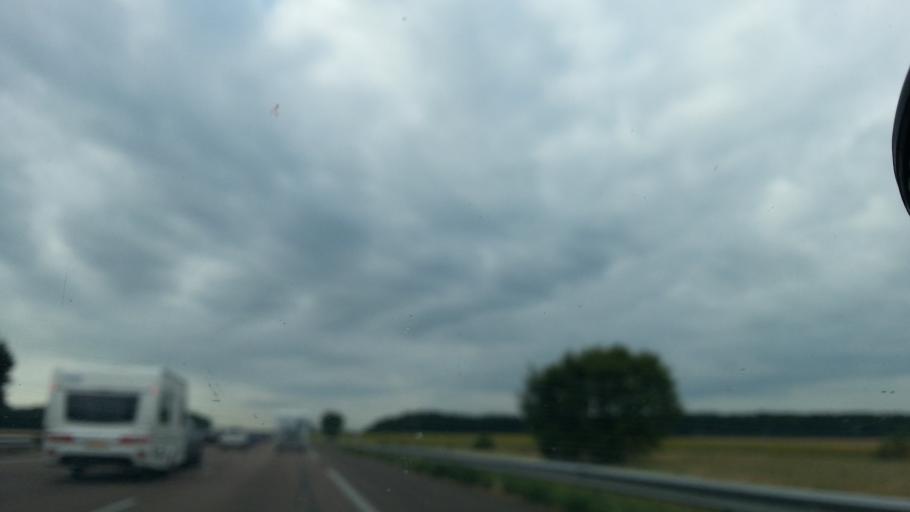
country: FR
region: Bourgogne
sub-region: Departement de Saone-et-Loire
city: Demigny
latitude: 46.9139
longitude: 4.8192
